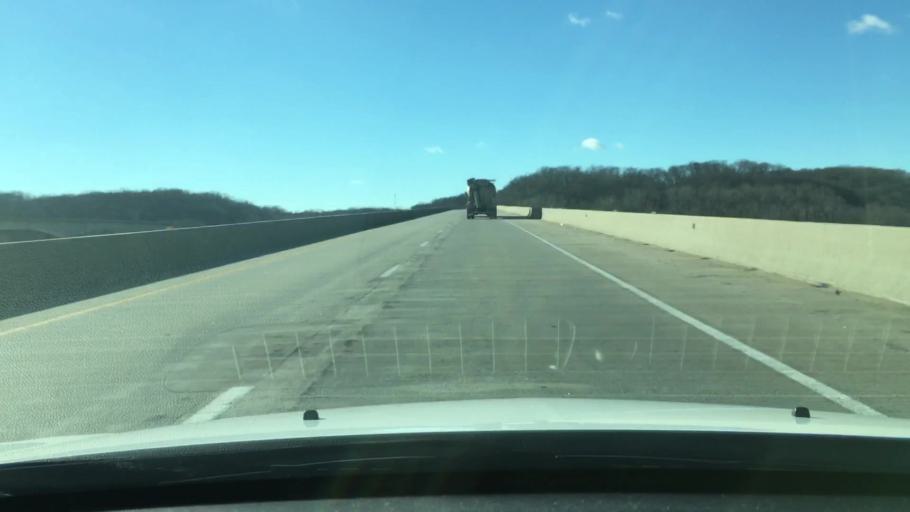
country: US
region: Illinois
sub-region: Pike County
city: Griggsville
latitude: 39.6901
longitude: -90.6363
